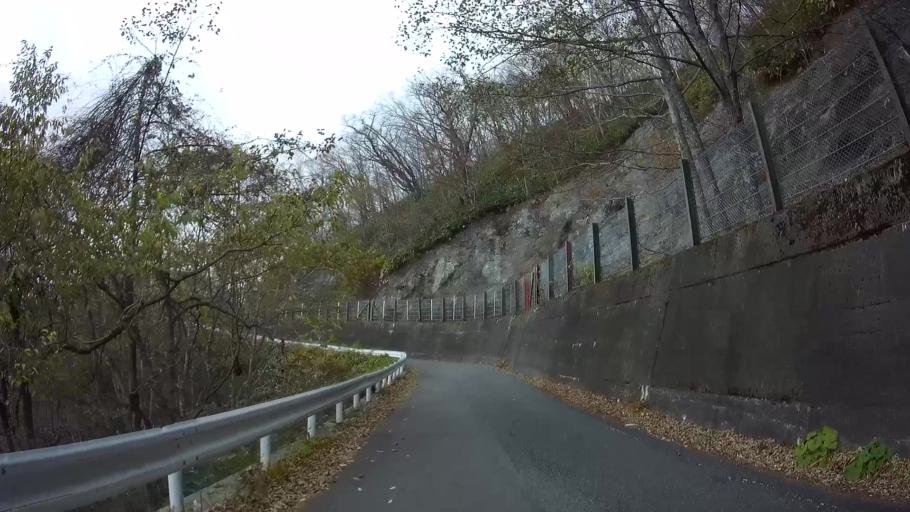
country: JP
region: Gunma
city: Nakanojomachi
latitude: 36.6862
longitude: 138.6577
